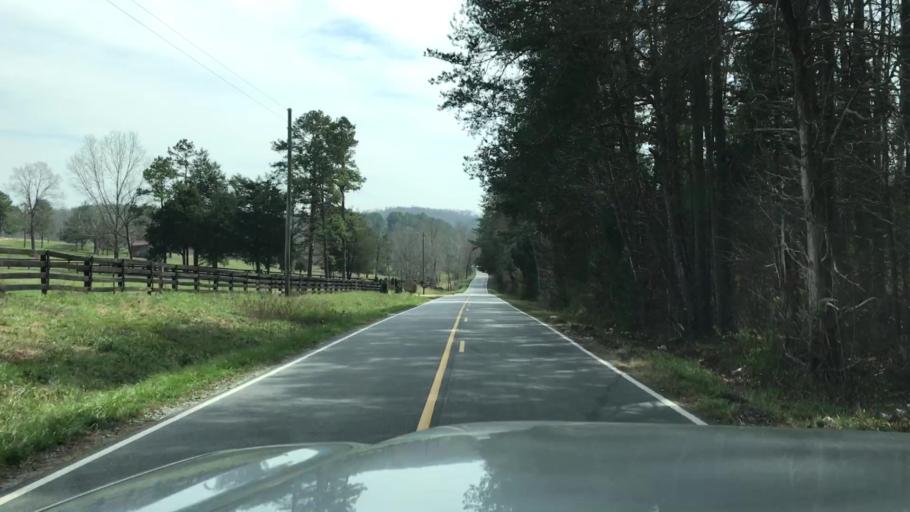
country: US
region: North Carolina
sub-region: Rutherford County
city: Spindale
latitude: 35.4536
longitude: -81.8834
